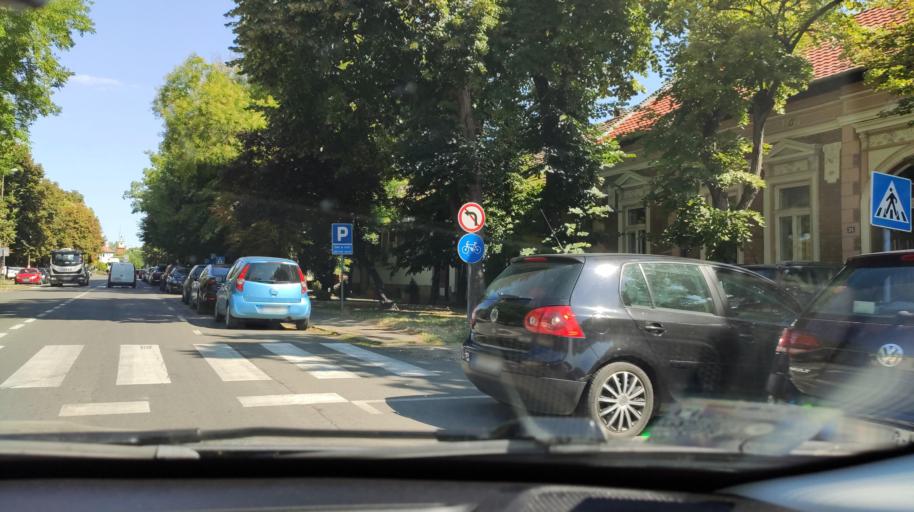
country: RS
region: Autonomna Pokrajina Vojvodina
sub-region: Severnobacki Okrug
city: Backa Topola
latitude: 45.8108
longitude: 19.6306
